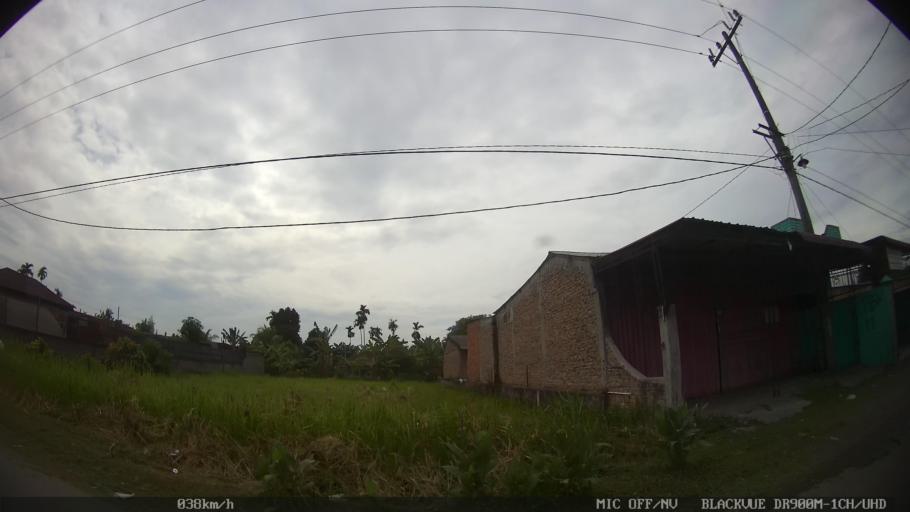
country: ID
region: North Sumatra
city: Sunggal
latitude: 3.6490
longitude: 98.5940
